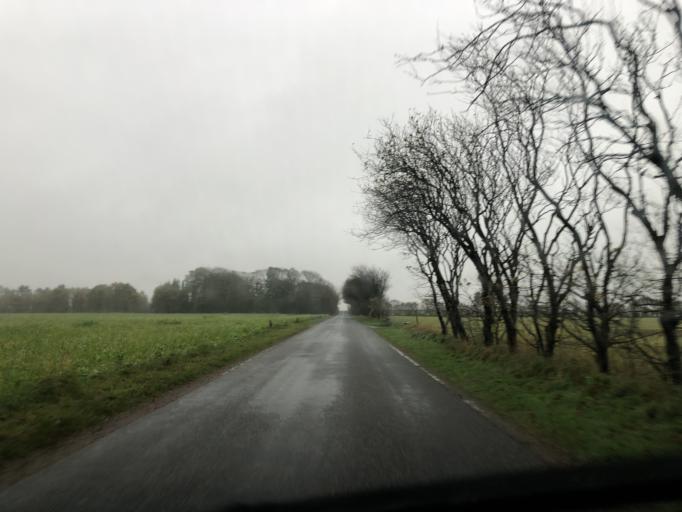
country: DK
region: Central Jutland
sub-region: Herning Kommune
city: Snejbjerg
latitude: 56.0861
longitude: 8.9123
